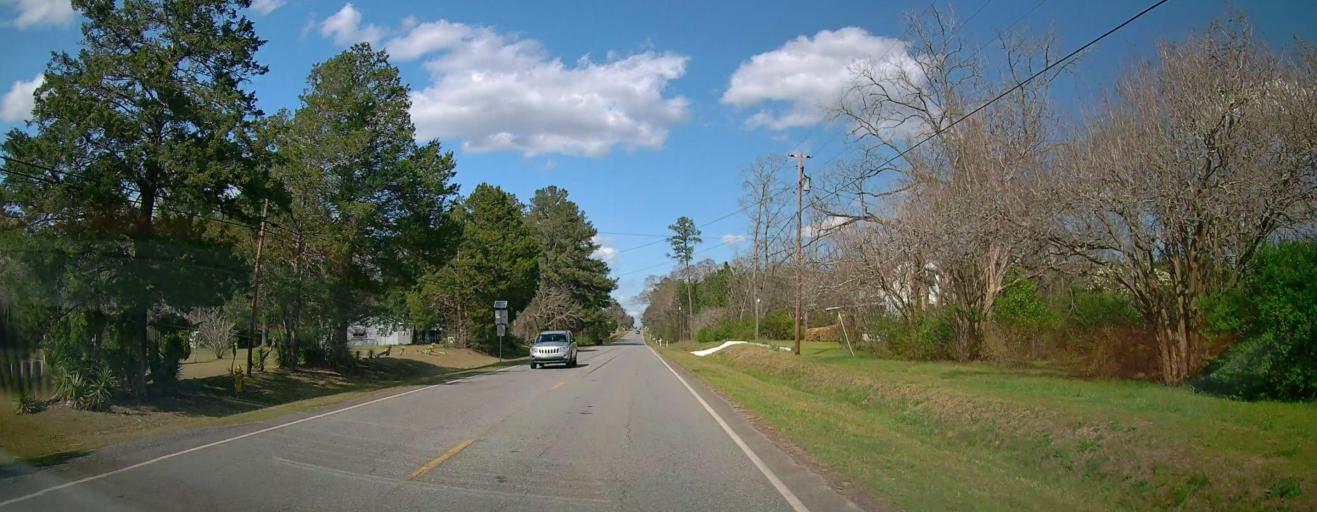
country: US
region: Georgia
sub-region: Baldwin County
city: Hardwick
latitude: 32.9778
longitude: -83.2784
